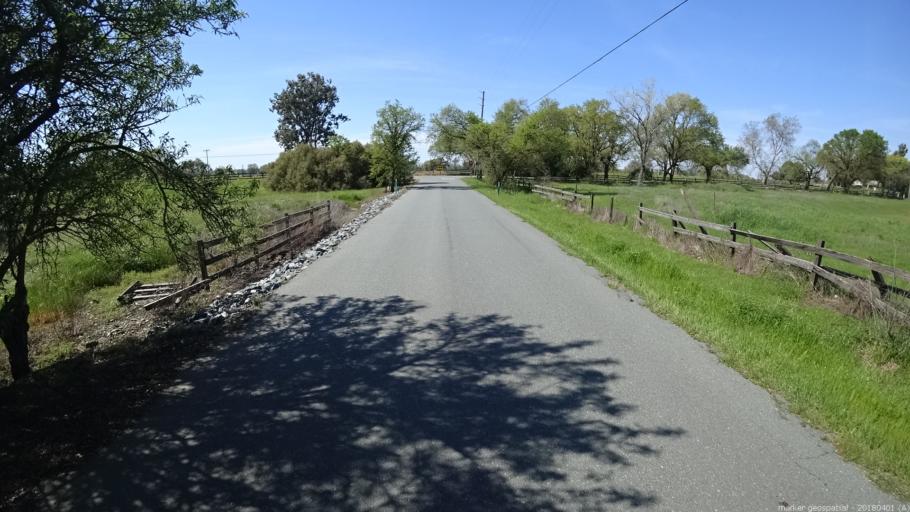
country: US
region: California
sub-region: Sacramento County
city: Wilton
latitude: 38.4148
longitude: -121.2548
